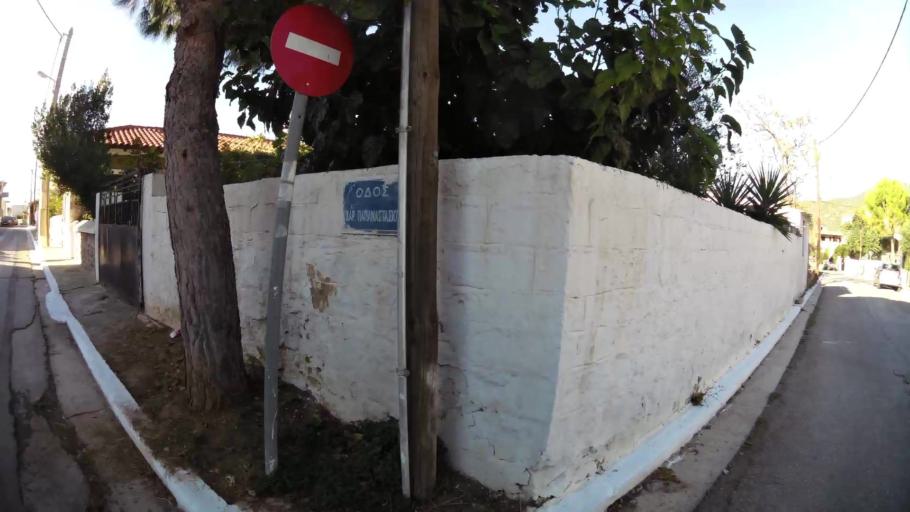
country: GR
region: Attica
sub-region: Nomarchia Anatolikis Attikis
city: Kalyvia Thorikou
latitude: 37.8390
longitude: 23.9304
